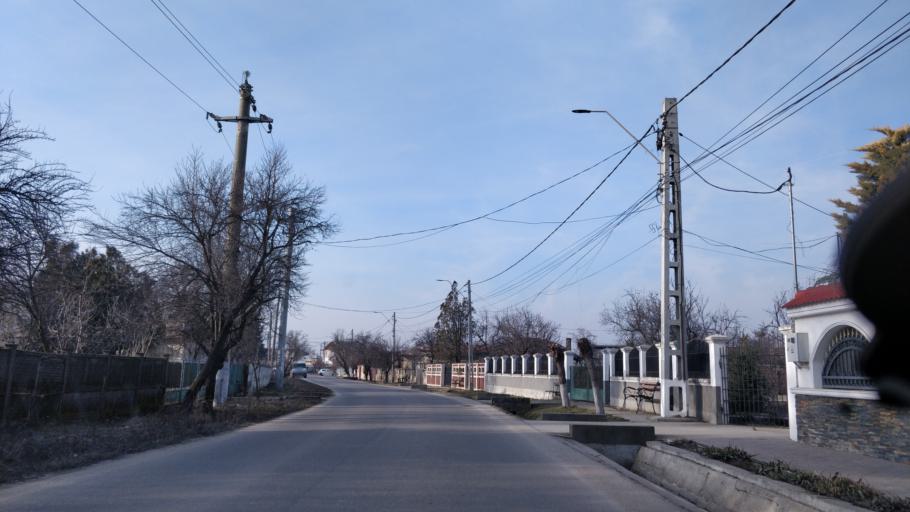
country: RO
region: Giurgiu
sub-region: Comuna Ulmi
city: Ulmi
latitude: 44.4817
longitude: 25.8058
